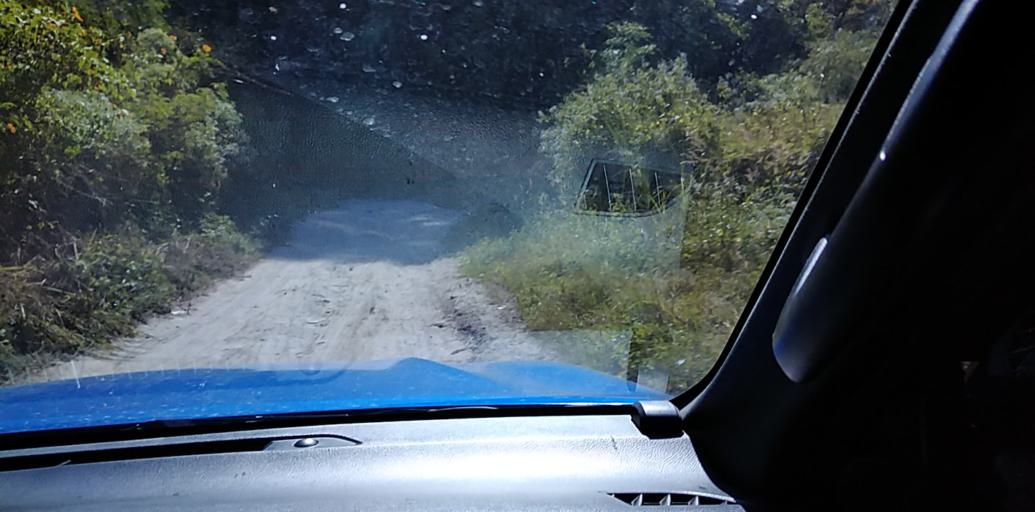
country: PH
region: Central Luzon
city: Santol
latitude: 15.1715
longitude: 120.4756
